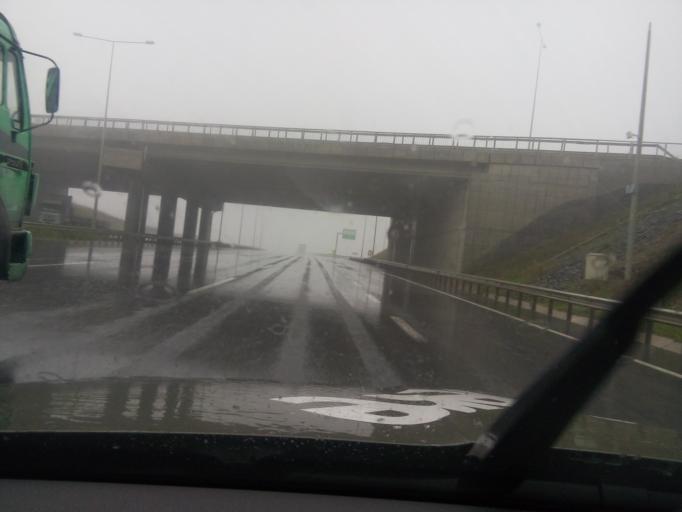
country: TR
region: Istanbul
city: Basaksehir
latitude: 41.1393
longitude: 28.8057
